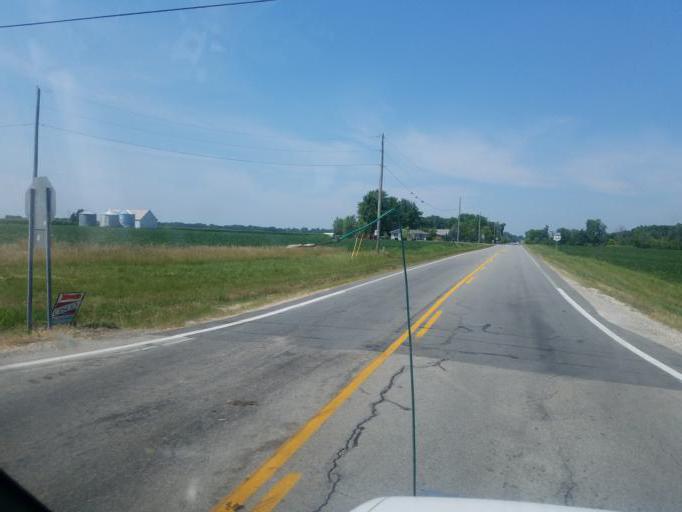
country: US
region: Ohio
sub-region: Auglaize County
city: Saint Marys
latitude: 40.4951
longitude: -84.4345
